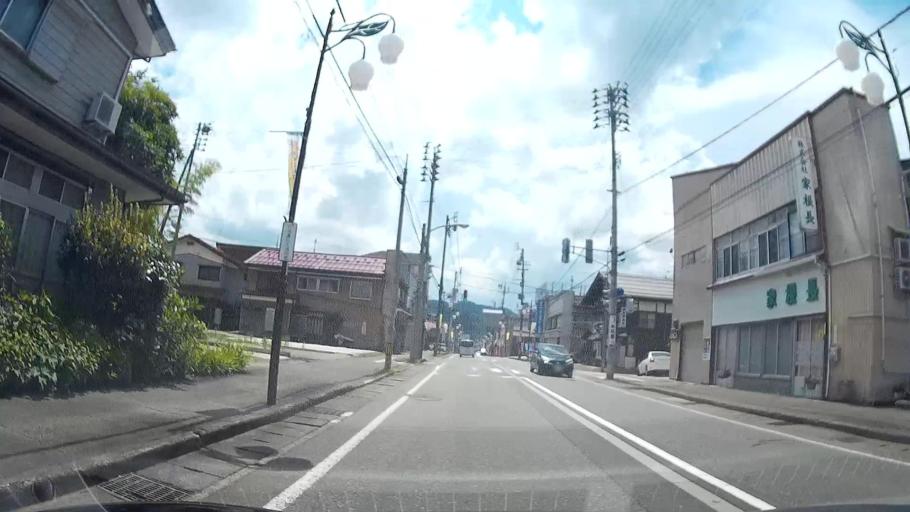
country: JP
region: Niigata
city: Tokamachi
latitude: 37.0158
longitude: 138.6534
